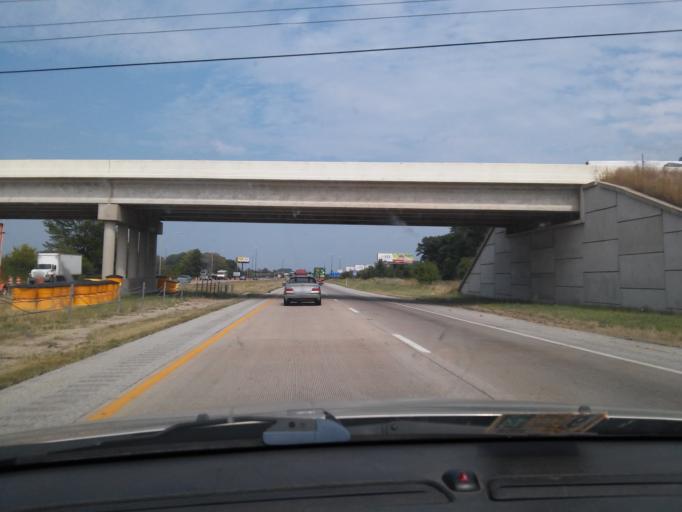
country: US
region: Indiana
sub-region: Wayne County
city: Richmond
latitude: 39.8654
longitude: -84.9396
